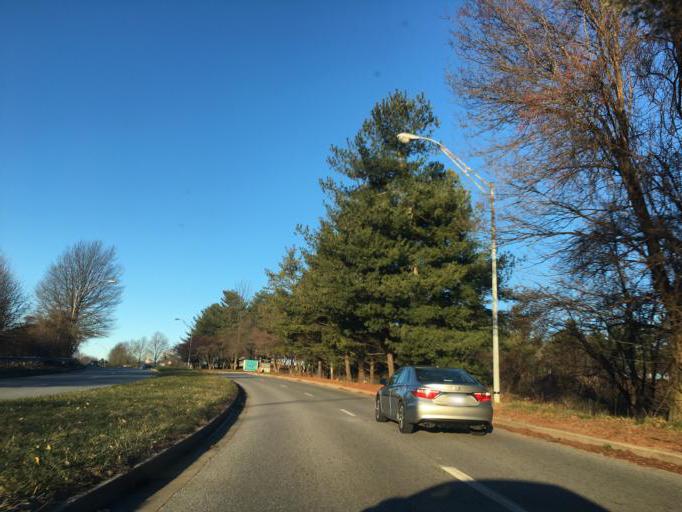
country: US
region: Maryland
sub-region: Baltimore County
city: Owings Mills
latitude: 39.4040
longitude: -76.7855
